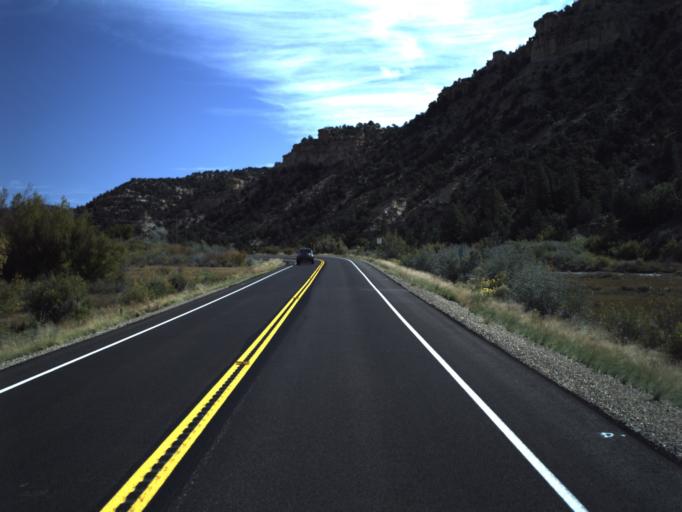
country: US
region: Utah
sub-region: Garfield County
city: Panguitch
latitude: 37.6038
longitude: -111.9128
